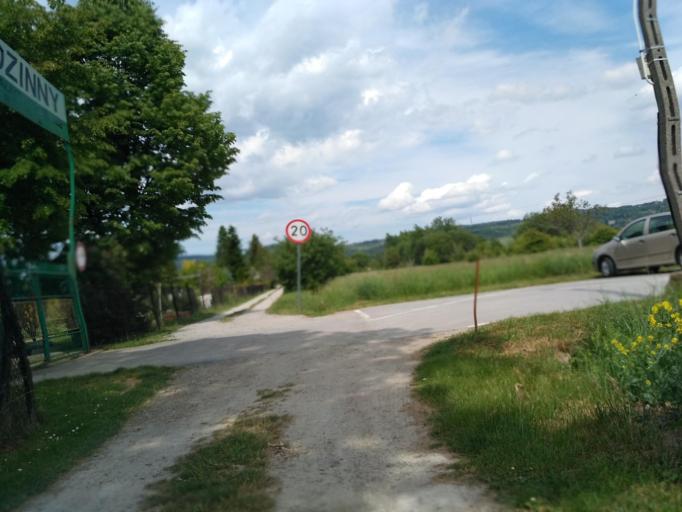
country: PL
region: Subcarpathian Voivodeship
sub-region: Powiat krosnienski
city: Odrzykon
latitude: 49.7177
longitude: 21.7566
